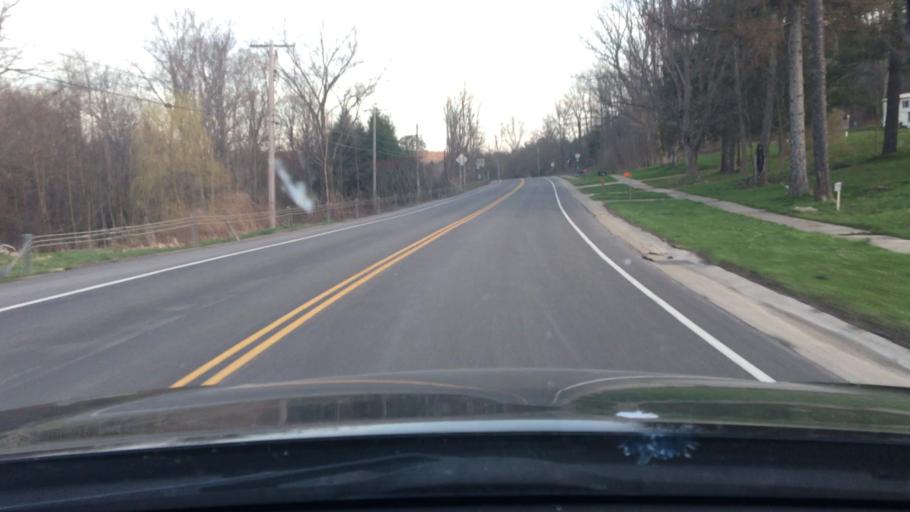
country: US
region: New York
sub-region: Cattaraugus County
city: Randolph
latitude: 42.1706
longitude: -78.9392
